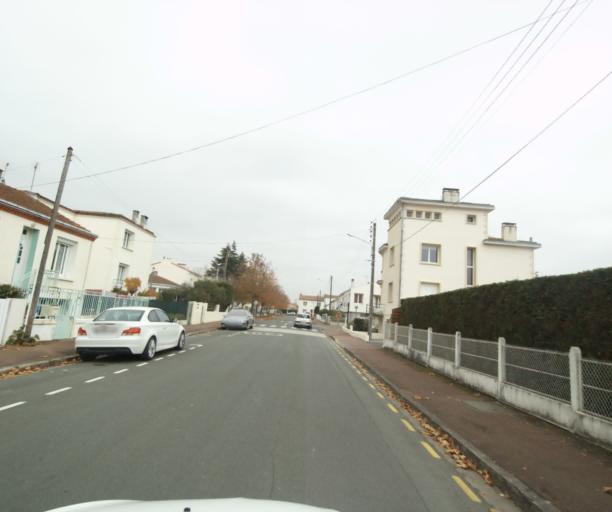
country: FR
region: Poitou-Charentes
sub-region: Departement de la Charente-Maritime
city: Saintes
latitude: 45.7429
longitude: -0.6218
